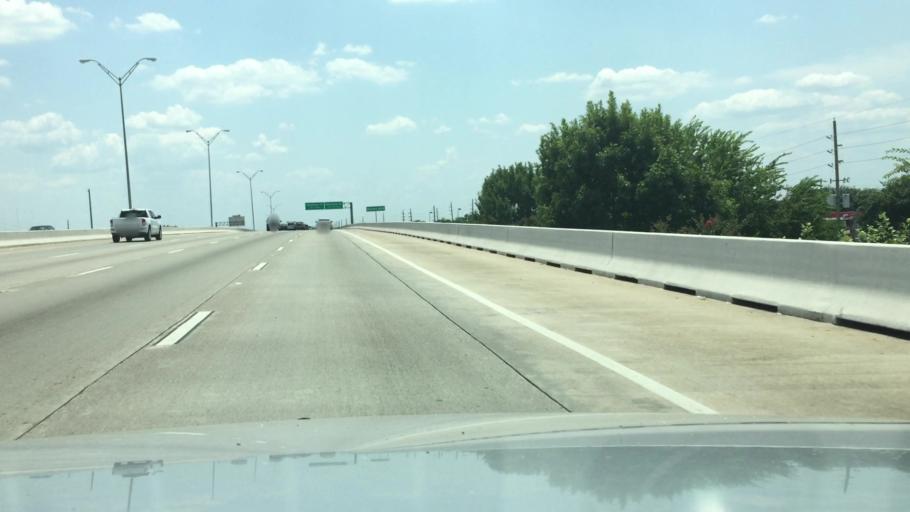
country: US
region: Texas
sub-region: Fort Bend County
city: Meadows Place
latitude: 29.7054
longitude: -95.5574
